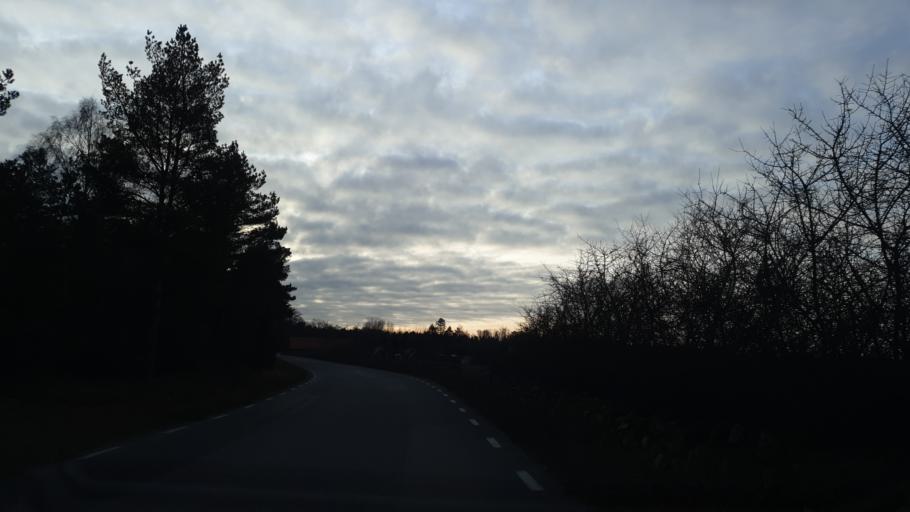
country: SE
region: Blekinge
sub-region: Karlskrona Kommun
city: Jaemjoe
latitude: 56.2135
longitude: 15.9694
